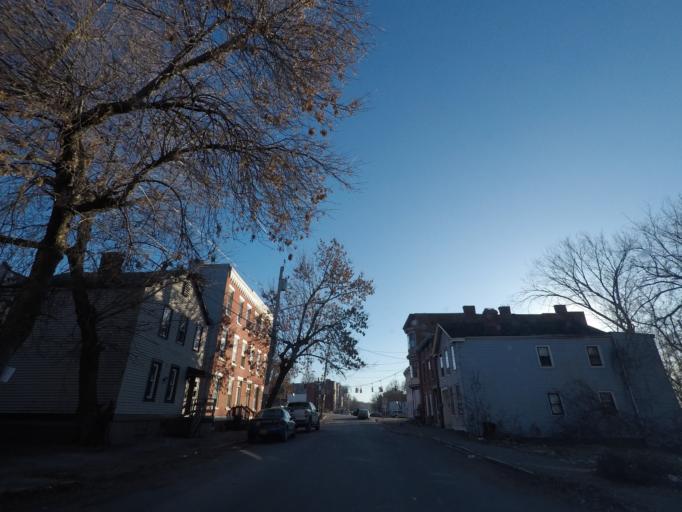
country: US
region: New York
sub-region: Albany County
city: Green Island
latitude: 42.7404
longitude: -73.6814
